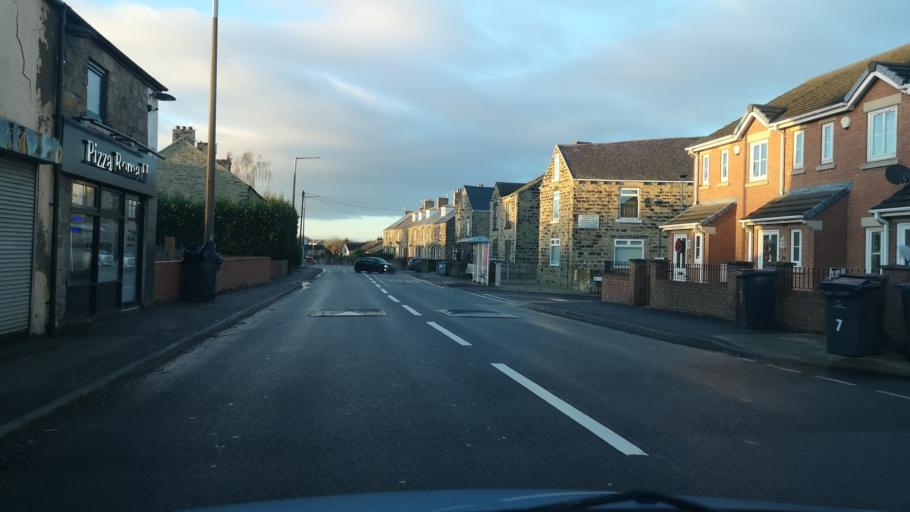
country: GB
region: England
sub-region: Barnsley
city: Great Houghton
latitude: 53.5552
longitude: -1.3529
